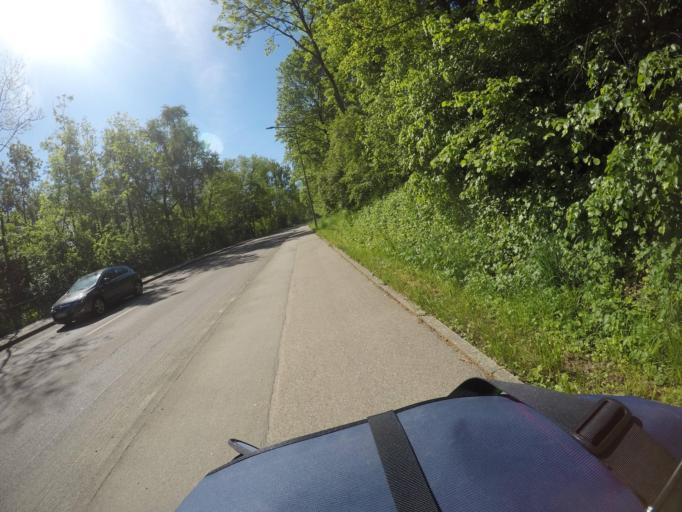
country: DE
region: Baden-Wuerttemberg
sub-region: Regierungsbezirk Stuttgart
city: Aalen
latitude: 48.8617
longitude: 10.0987
